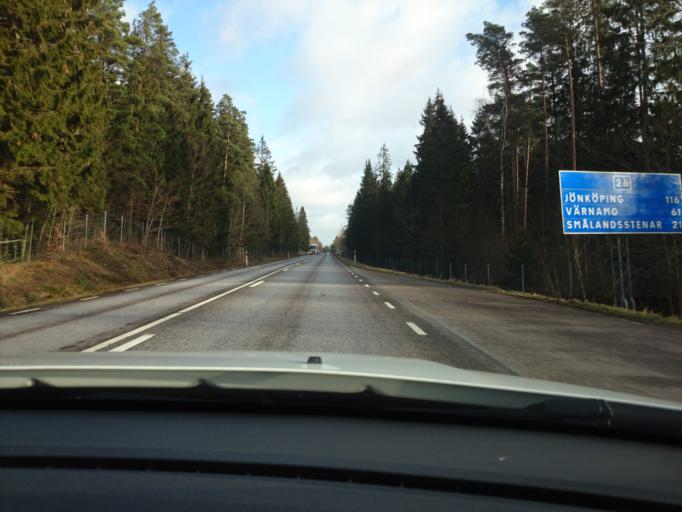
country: SE
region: Halland
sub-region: Hylte Kommun
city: Hyltebruk
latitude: 57.0206
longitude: 13.2487
